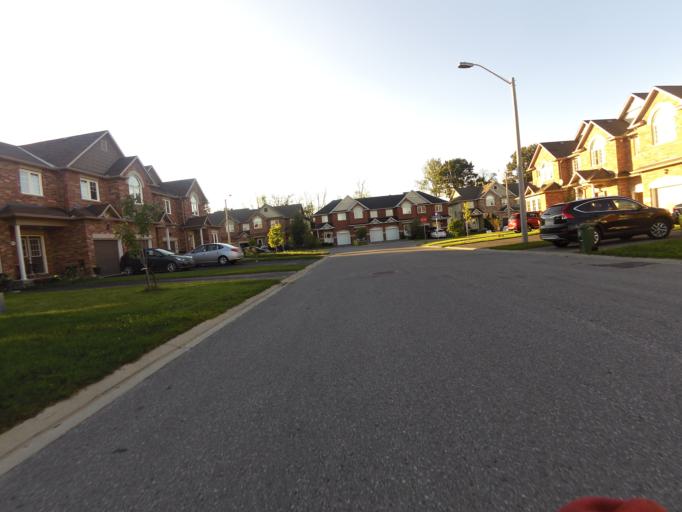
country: CA
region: Ontario
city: Bells Corners
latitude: 45.3626
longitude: -75.9309
